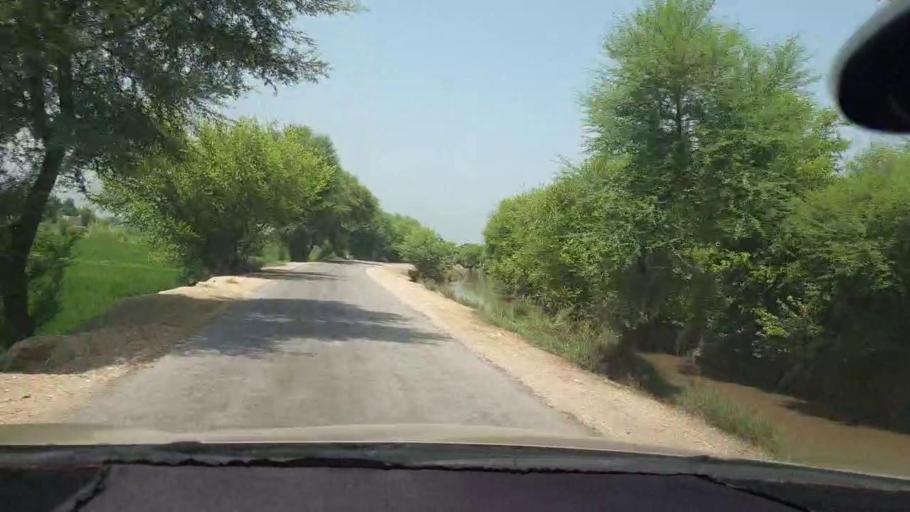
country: PK
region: Sindh
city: Kambar
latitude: 27.6473
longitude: 67.9695
